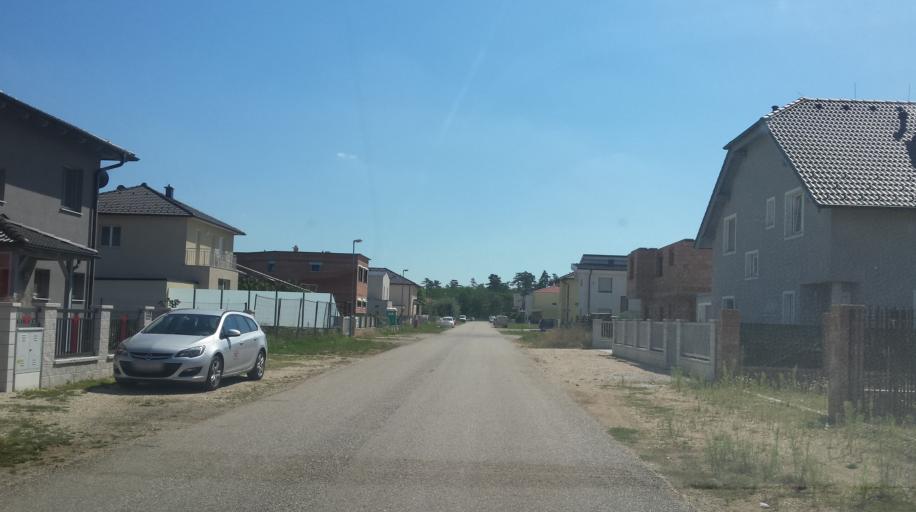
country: AT
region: Lower Austria
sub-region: Politischer Bezirk Ganserndorf
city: Strasshof an der Nordbahn
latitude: 48.3111
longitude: 16.6285
